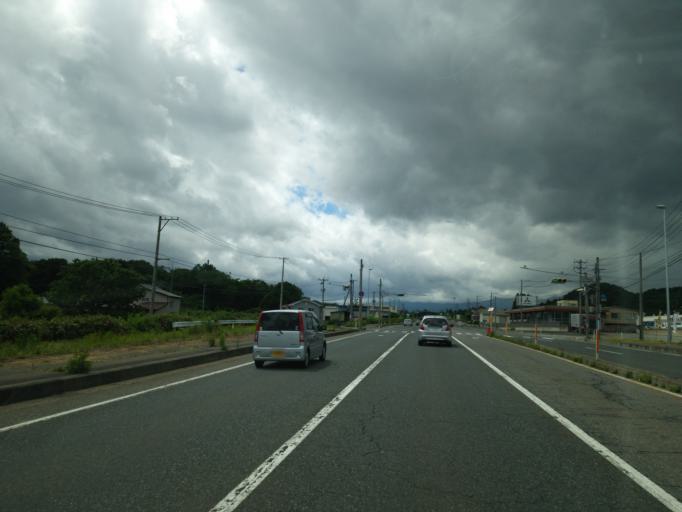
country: JP
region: Iwate
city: Shizukuishi
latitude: 39.6998
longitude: 141.0543
